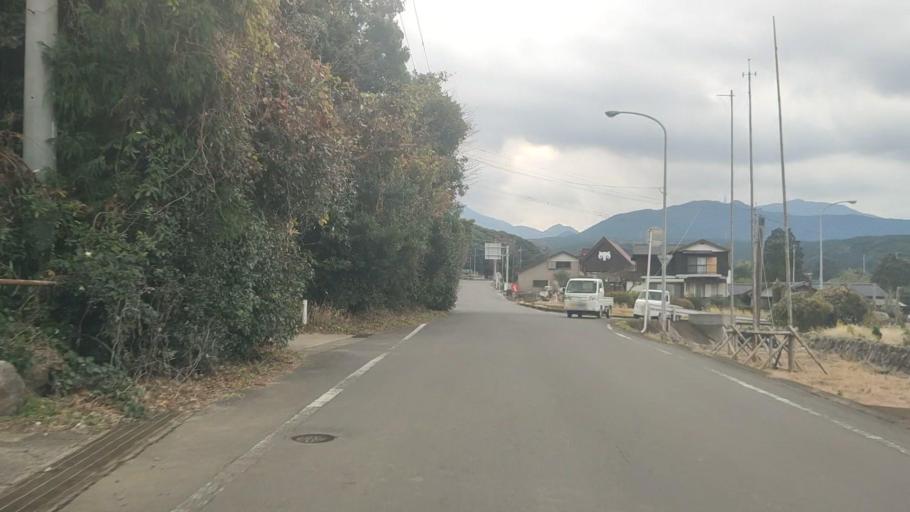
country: JP
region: Nagasaki
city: Shimabara
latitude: 32.8267
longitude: 130.2919
